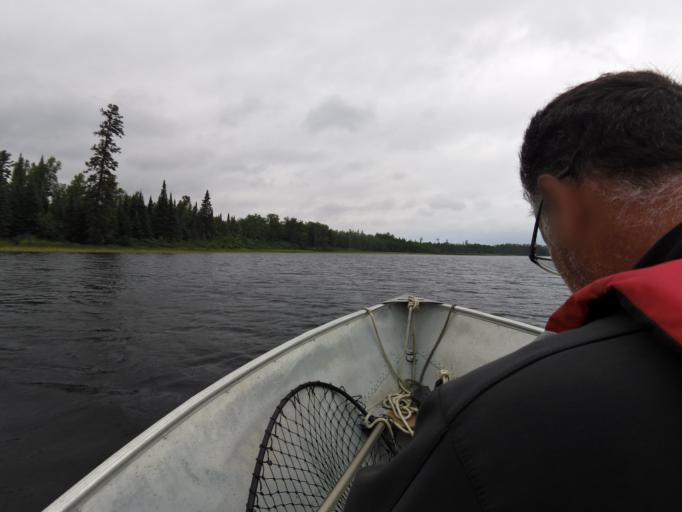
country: CA
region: Ontario
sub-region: Rainy River District
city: Atikokan
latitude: 49.5949
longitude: -91.3570
